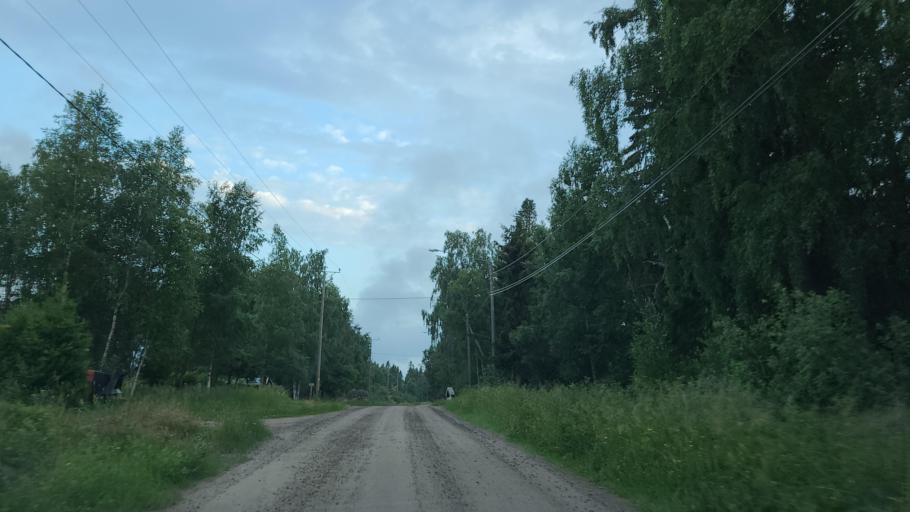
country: FI
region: Ostrobothnia
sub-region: Vaasa
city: Replot
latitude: 63.3129
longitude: 21.1600
